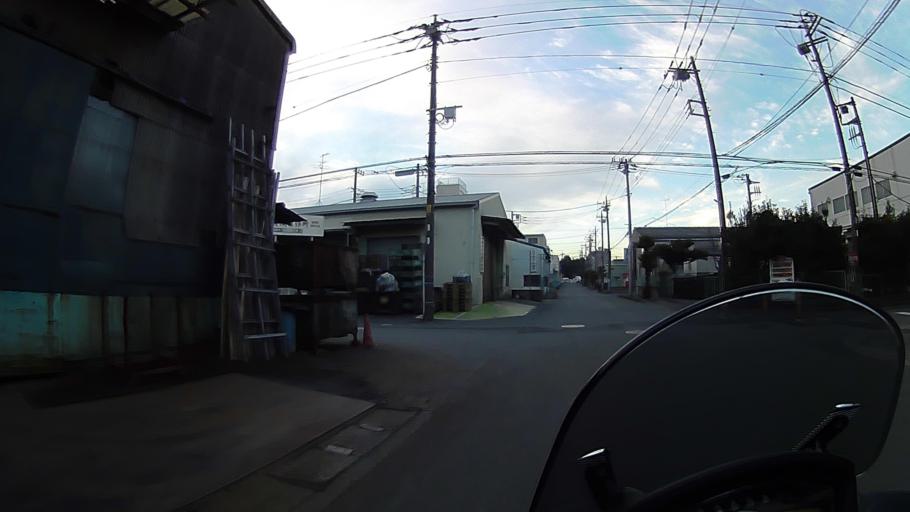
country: JP
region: Kanagawa
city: Atsugi
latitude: 35.4257
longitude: 139.4216
